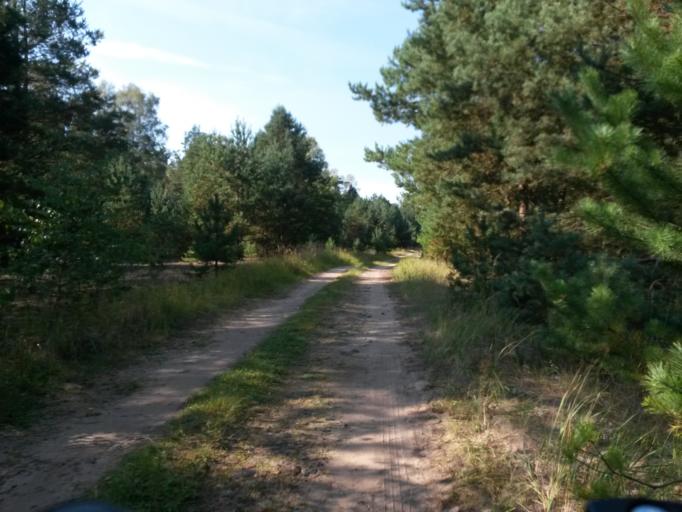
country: DE
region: Brandenburg
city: Templin
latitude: 53.0770
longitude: 13.3942
